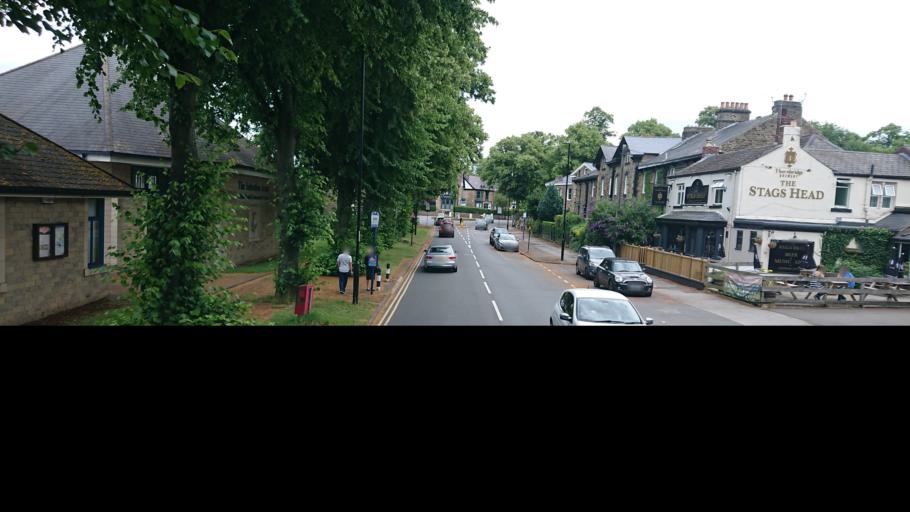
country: GB
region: England
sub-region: Sheffield
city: Sheffield
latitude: 53.3668
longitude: -1.4905
